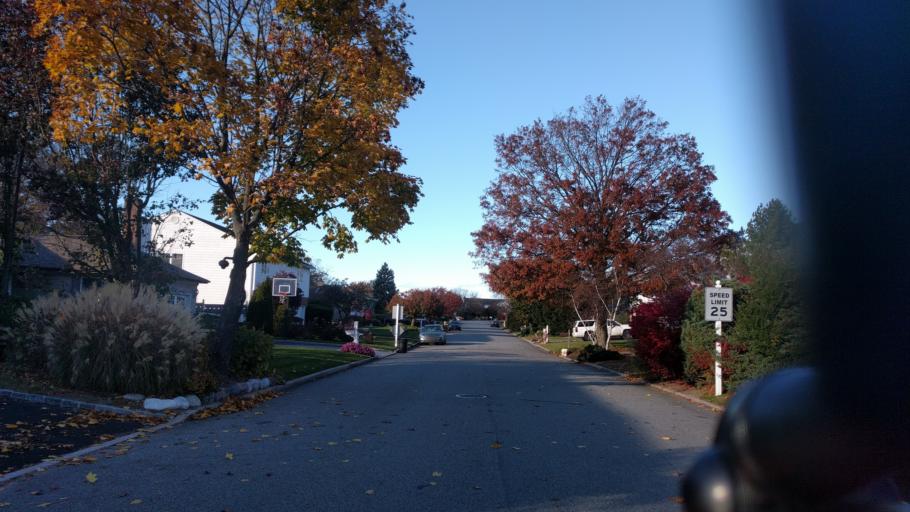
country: US
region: New York
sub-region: Nassau County
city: Bayville
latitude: 40.9127
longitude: -73.5664
